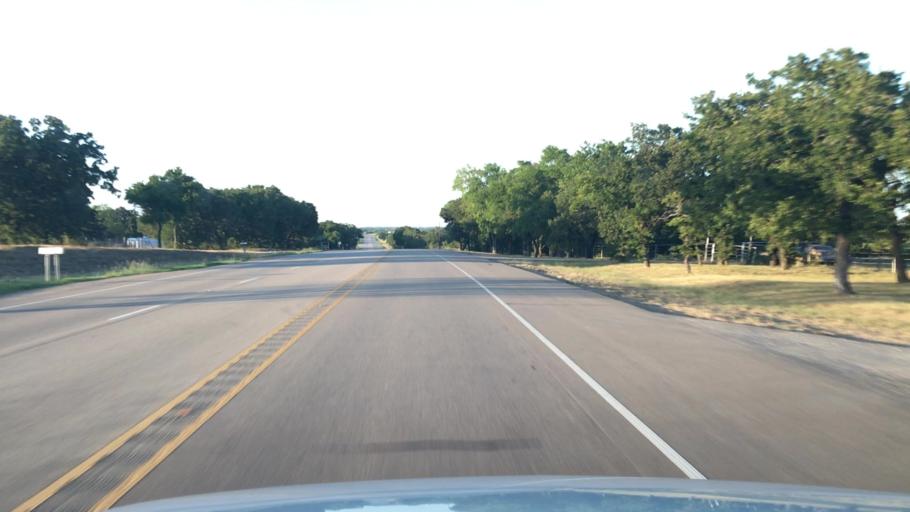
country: US
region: Texas
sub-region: Hamilton County
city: Hico
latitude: 31.9501
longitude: -98.0484
